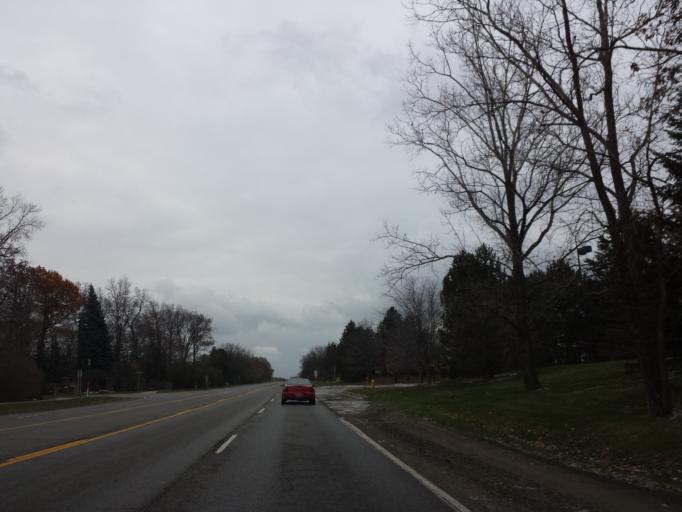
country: US
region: Michigan
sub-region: Oakland County
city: Bloomfield Hills
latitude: 42.6175
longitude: -83.2486
